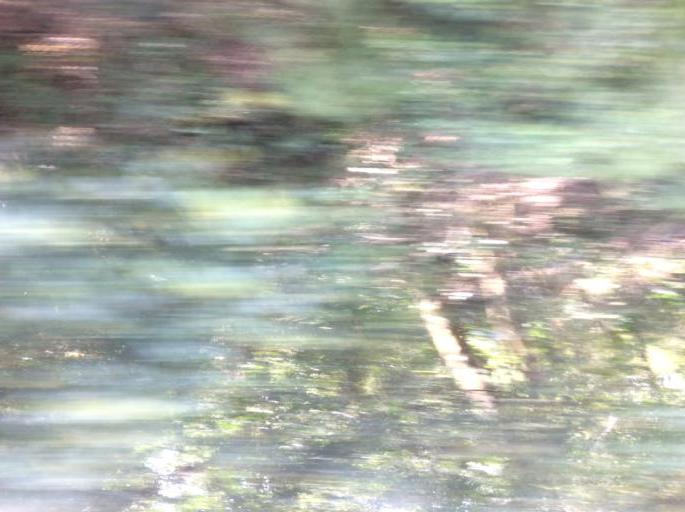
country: TW
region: Taipei
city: Taipei
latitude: 25.1592
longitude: 121.5465
